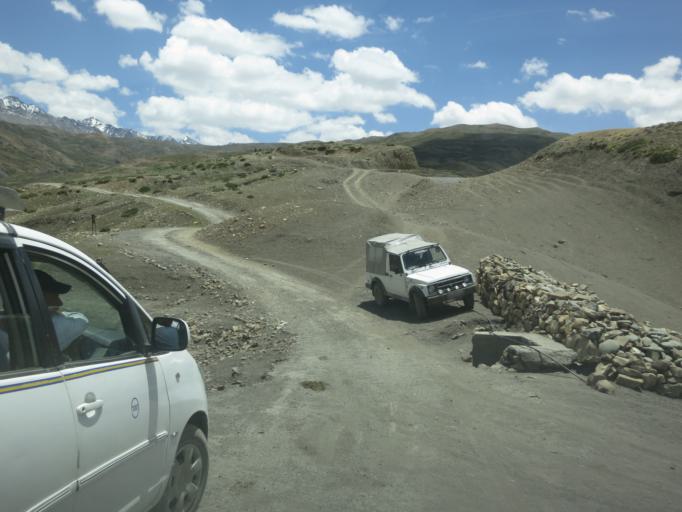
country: IN
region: Himachal Pradesh
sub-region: Shimla
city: Sarahan
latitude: 32.2769
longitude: 78.0871
